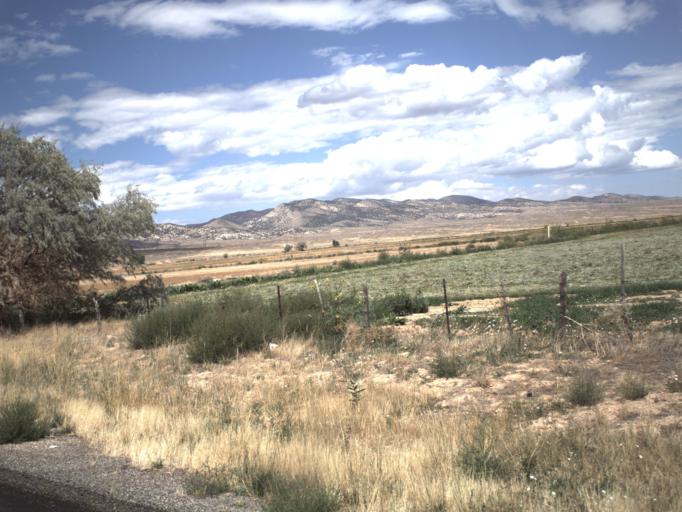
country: US
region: Utah
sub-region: Sevier County
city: Aurora
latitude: 38.9553
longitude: -111.9133
